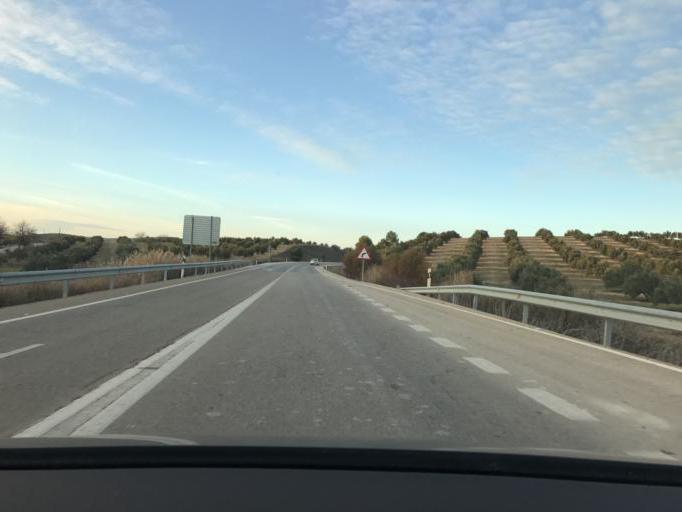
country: ES
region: Andalusia
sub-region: Provincia de Jaen
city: Ubeda
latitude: 37.9284
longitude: -3.3545
